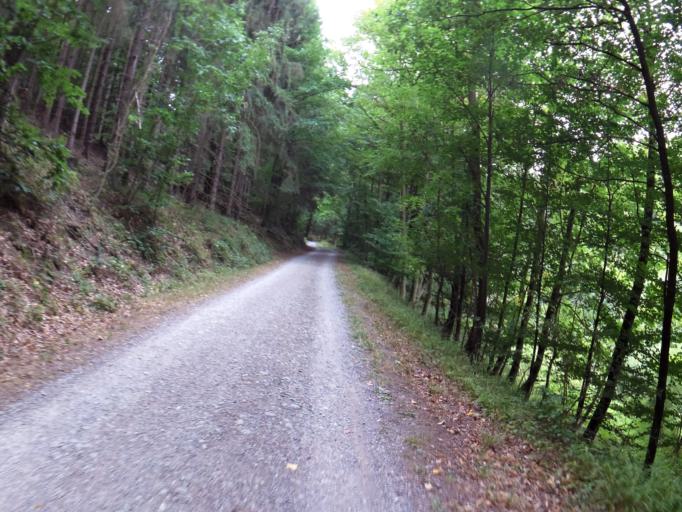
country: DE
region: North Rhine-Westphalia
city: Heimbach
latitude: 50.6296
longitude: 6.4206
